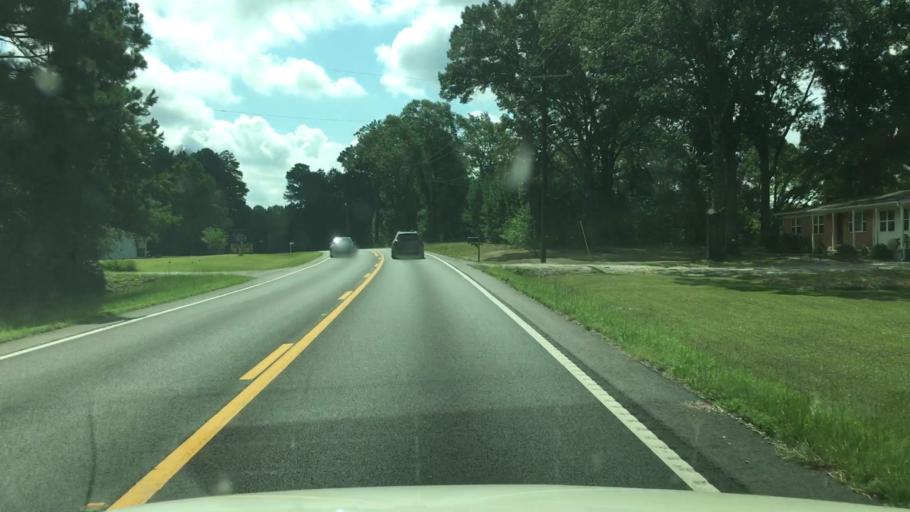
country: US
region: Arkansas
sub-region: Garland County
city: Lake Hamilton
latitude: 34.2794
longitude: -93.1581
